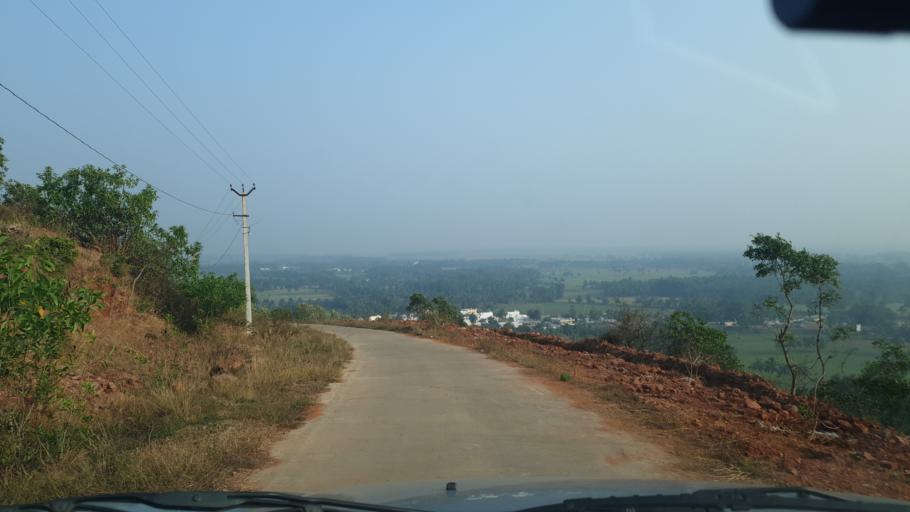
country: IN
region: Andhra Pradesh
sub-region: Srikakulam
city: Narasannapeta
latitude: 18.3324
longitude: 84.0341
